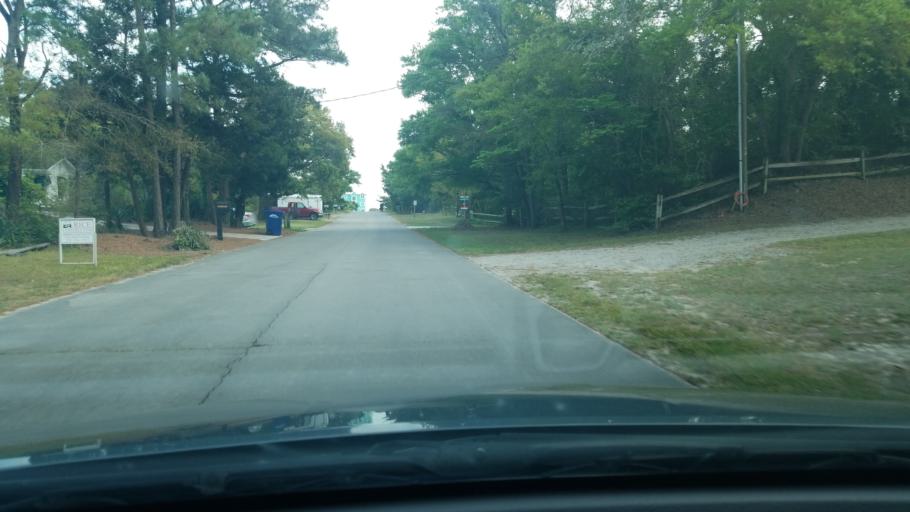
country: US
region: North Carolina
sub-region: Carteret County
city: Cape Carteret
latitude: 34.6614
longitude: -77.0453
